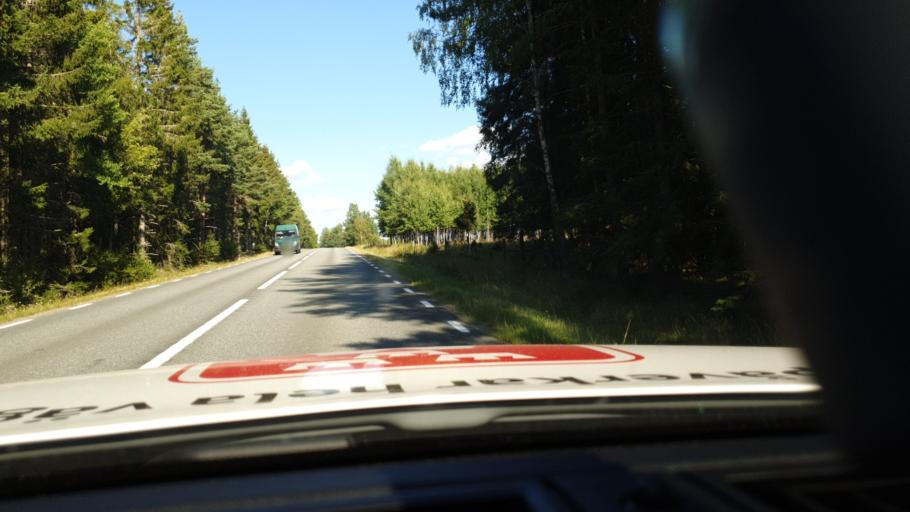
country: SE
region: Joenkoeping
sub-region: Eksjo Kommun
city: Eksjoe
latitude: 57.7305
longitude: 15.0416
